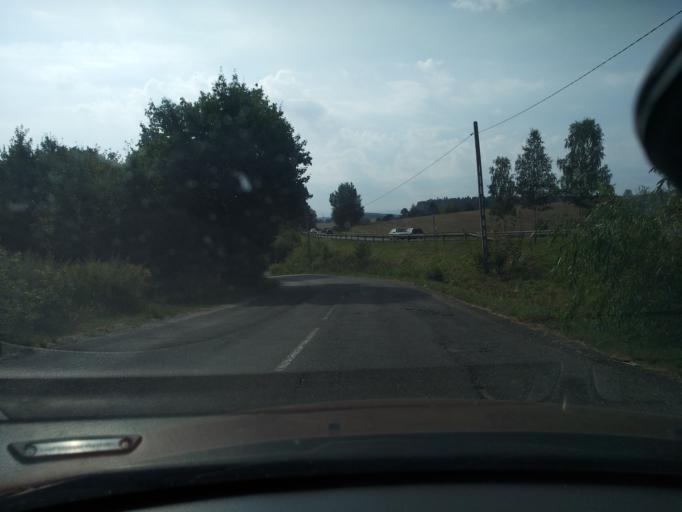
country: PL
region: Lower Silesian Voivodeship
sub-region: Powiat jeleniogorski
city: Stara Kamienica
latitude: 50.9416
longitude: 15.5931
